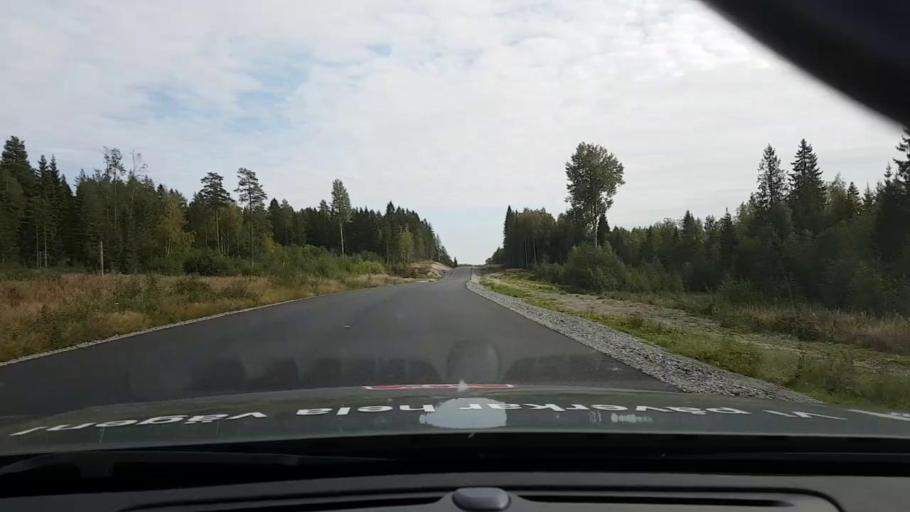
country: SE
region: Vaesternorrland
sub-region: OErnskoeldsviks Kommun
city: Bjasta
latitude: 63.2926
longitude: 18.4990
